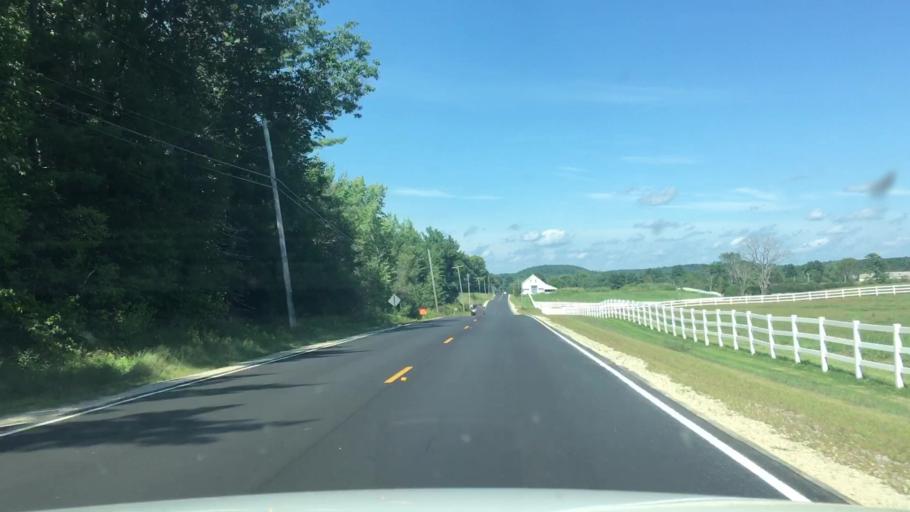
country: US
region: Maine
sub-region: Cumberland County
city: Cumberland Center
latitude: 43.7824
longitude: -70.3039
